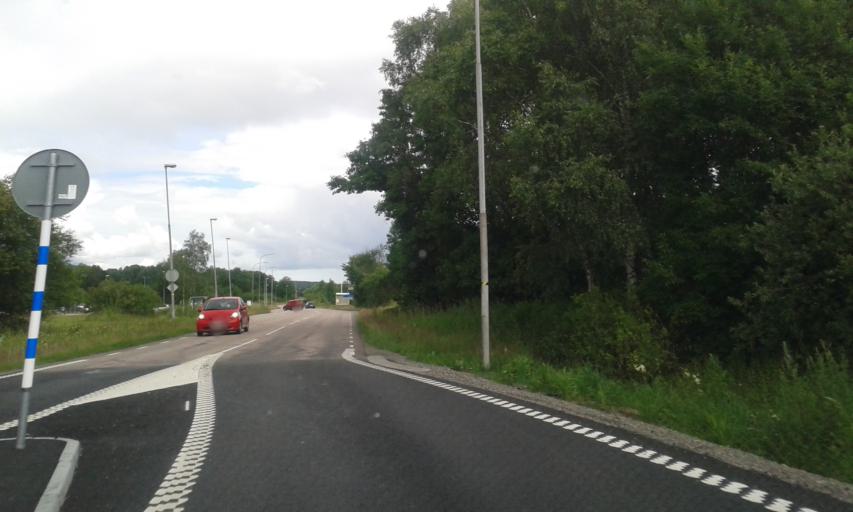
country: SE
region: Vaestra Goetaland
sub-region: Kungalvs Kommun
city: Diserod
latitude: 57.9225
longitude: 12.0308
